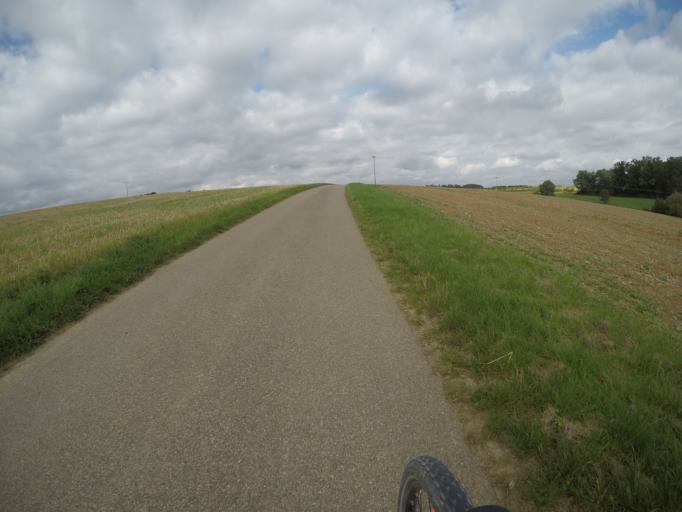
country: DE
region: Baden-Wuerttemberg
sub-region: Regierungsbezirk Stuttgart
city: Renningen
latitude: 48.7418
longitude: 8.9131
